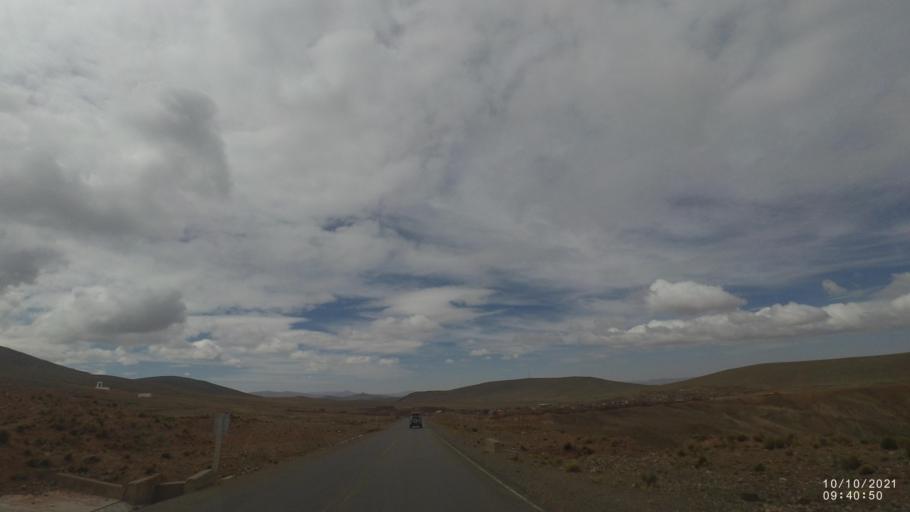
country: BO
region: La Paz
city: Quime
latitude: -17.1416
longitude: -67.3438
